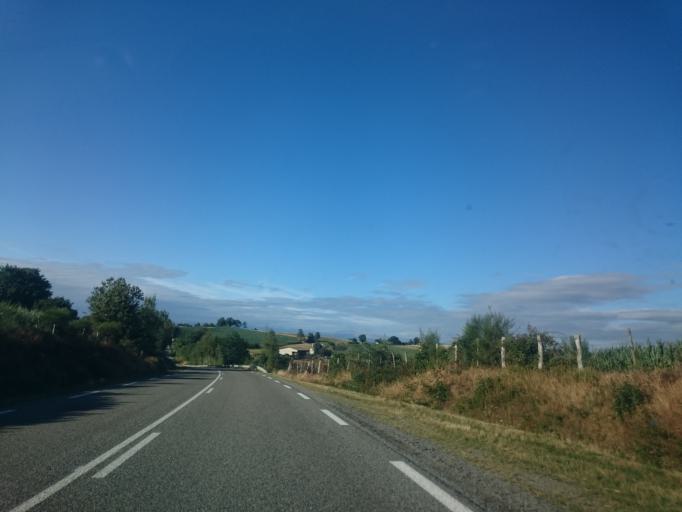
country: FR
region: Midi-Pyrenees
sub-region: Departement de l'Aveyron
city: Entraygues-sur-Truyere
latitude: 44.7259
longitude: 2.5072
